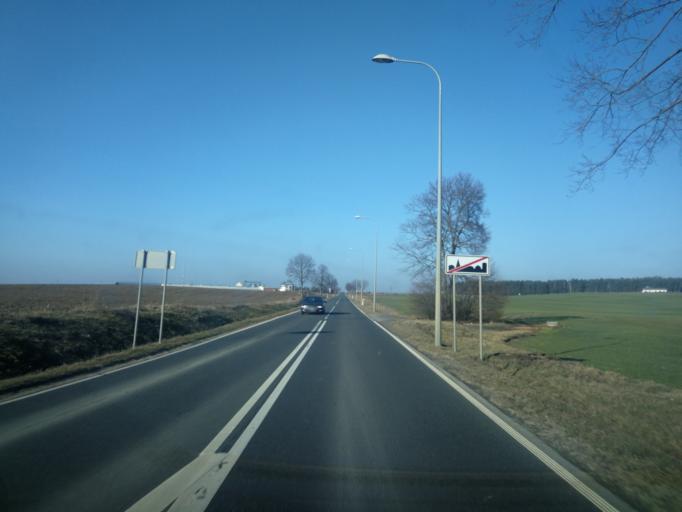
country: PL
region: Warmian-Masurian Voivodeship
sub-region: Powiat ilawski
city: Lubawa
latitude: 53.4303
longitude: 19.7739
